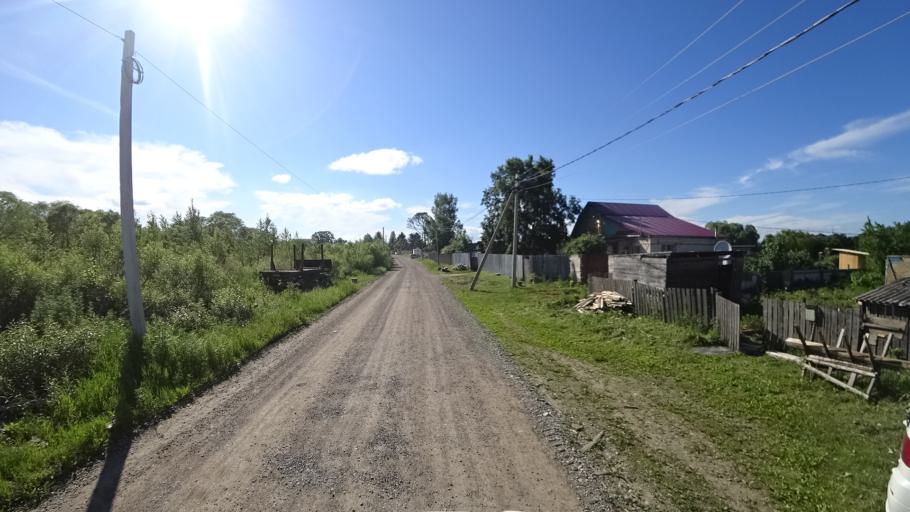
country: RU
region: Khabarovsk Krai
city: Khor
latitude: 47.8857
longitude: 135.0174
